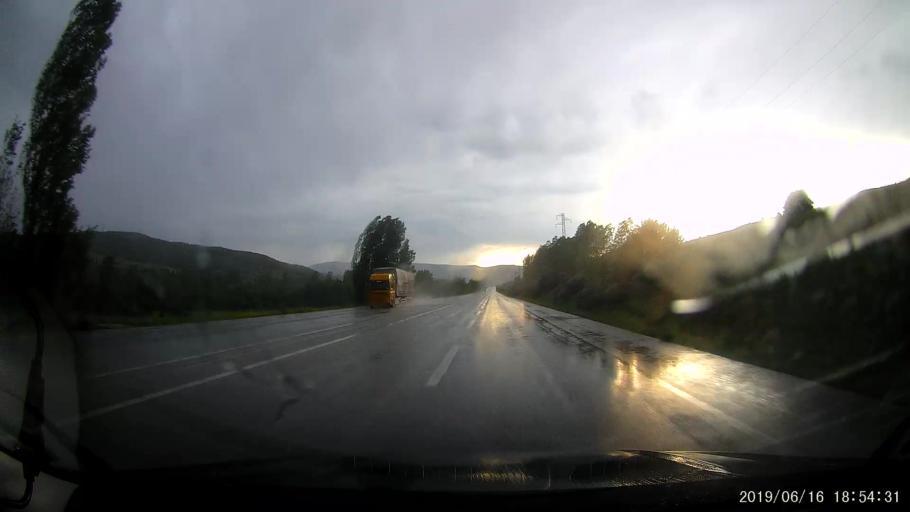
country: TR
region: Erzincan
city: Catalcam
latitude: 39.8972
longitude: 38.8517
